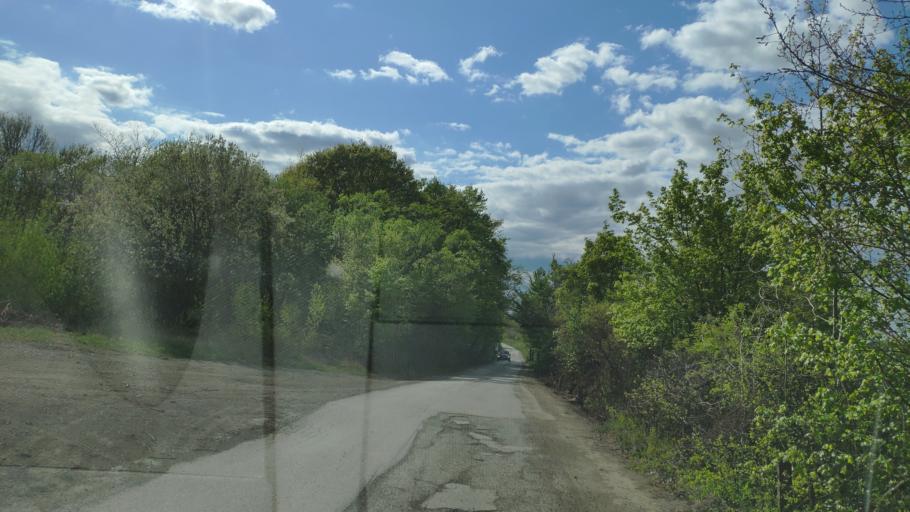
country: SK
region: Kosicky
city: Kosice
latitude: 48.6767
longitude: 21.4408
